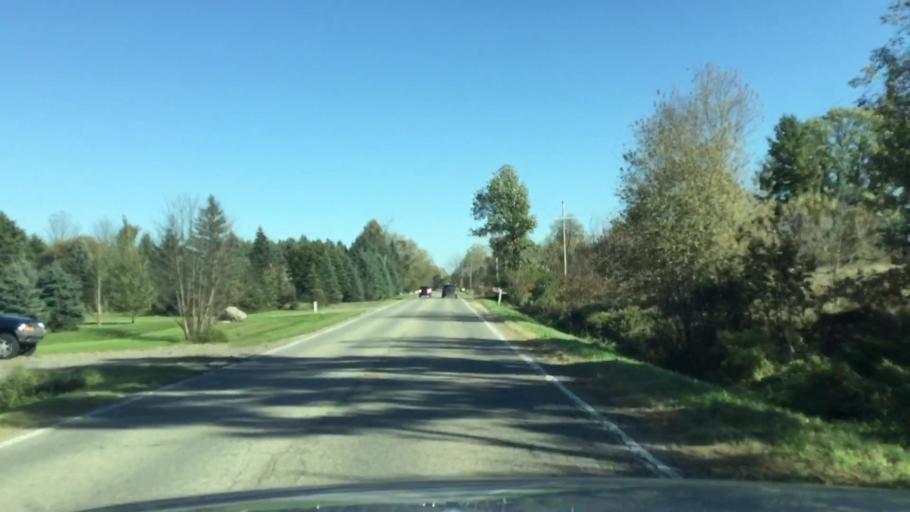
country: US
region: Michigan
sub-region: Lapeer County
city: Lapeer
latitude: 43.0722
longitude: -83.3300
